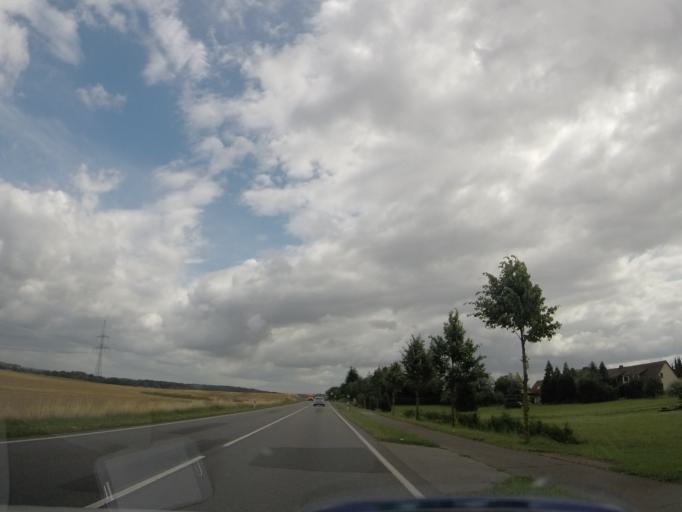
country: DE
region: Mecklenburg-Vorpommern
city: Lalendorf
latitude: 53.7641
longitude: 12.3530
